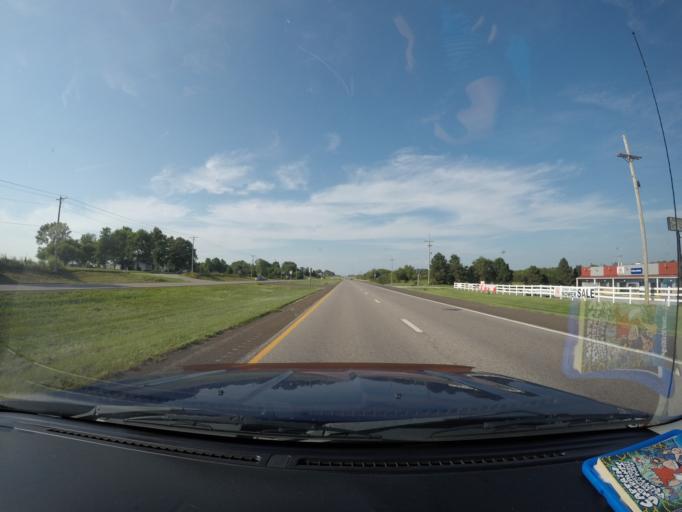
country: US
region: Kansas
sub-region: Leavenworth County
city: Basehor
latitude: 39.1809
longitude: -94.9003
